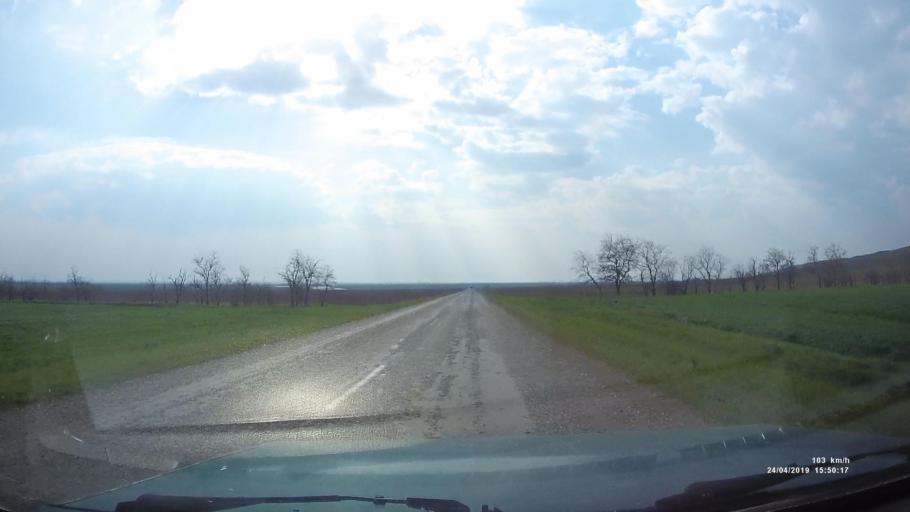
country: RU
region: Kalmykiya
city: Yashalta
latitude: 46.6041
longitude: 42.6363
